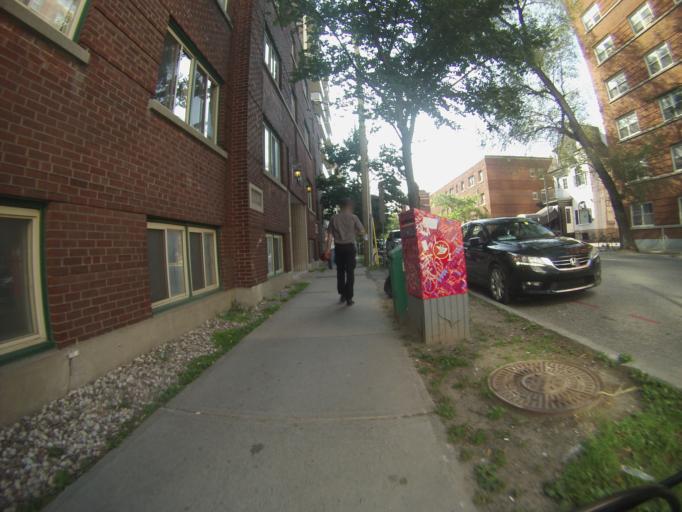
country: CA
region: Ontario
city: Ottawa
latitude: 45.4184
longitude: -75.6934
